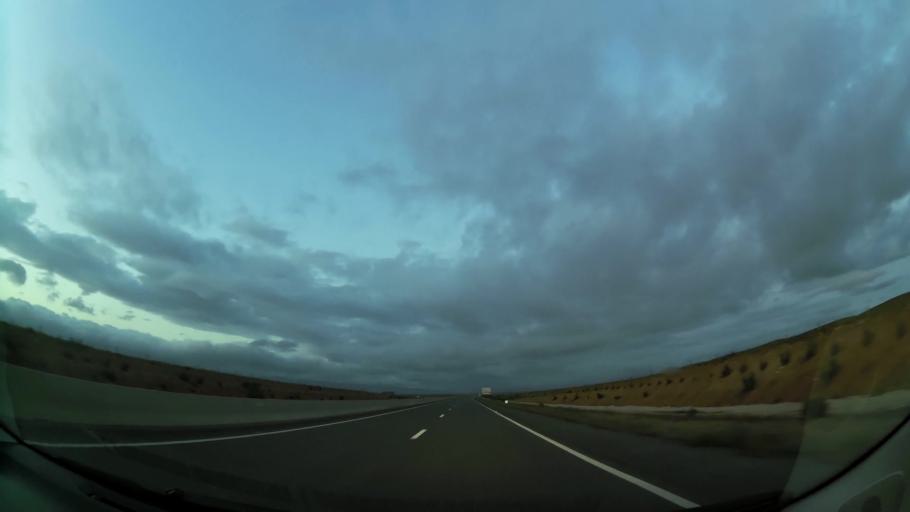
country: MA
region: Oriental
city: El Aioun
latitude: 34.6226
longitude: -2.3973
